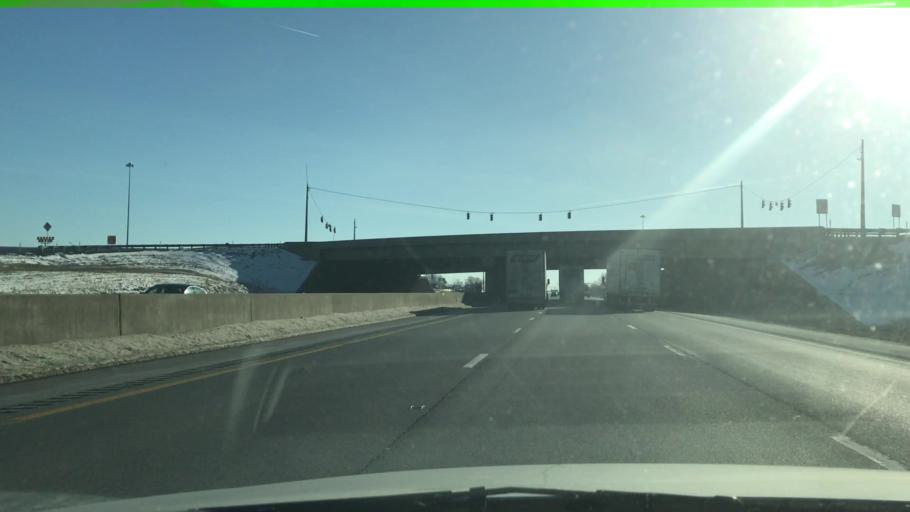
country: US
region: Kentucky
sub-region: Warren County
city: Plano
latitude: 36.9364
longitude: -86.4175
